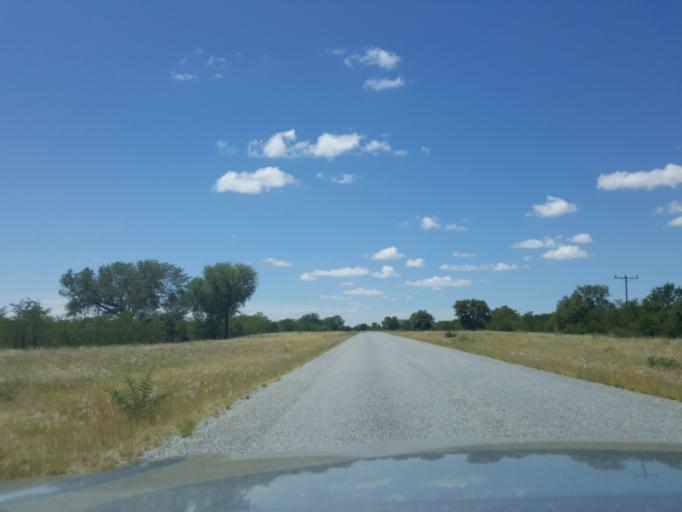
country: BW
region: Central
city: Nata
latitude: -20.1486
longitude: 25.7332
